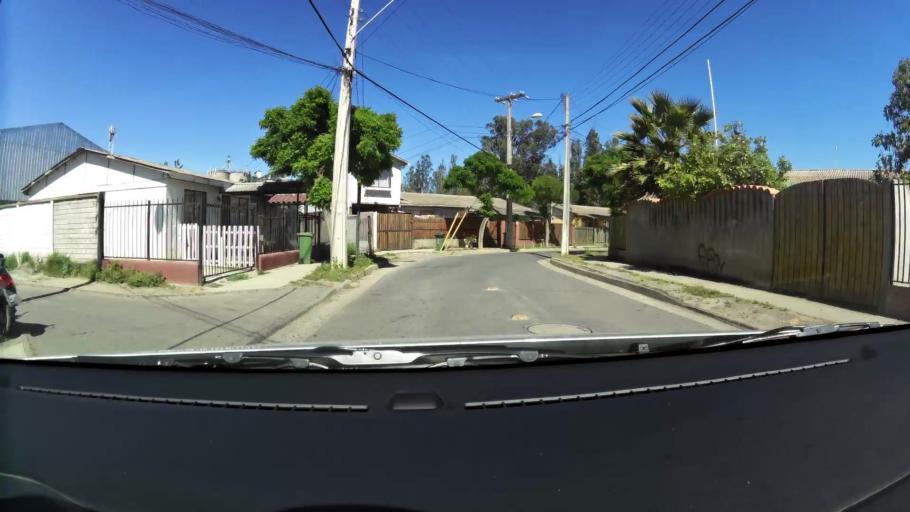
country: CL
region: Valparaiso
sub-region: Provincia de Marga Marga
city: Quilpue
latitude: -33.3117
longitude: -71.4103
